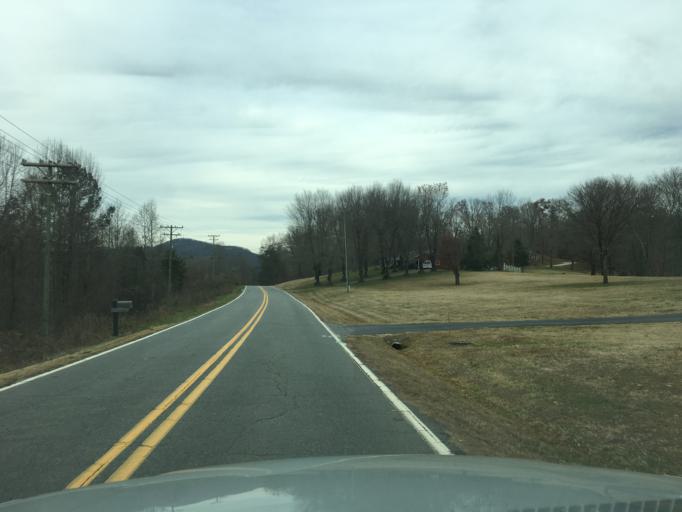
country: US
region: North Carolina
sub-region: McDowell County
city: West Marion
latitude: 35.6203
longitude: -81.9815
